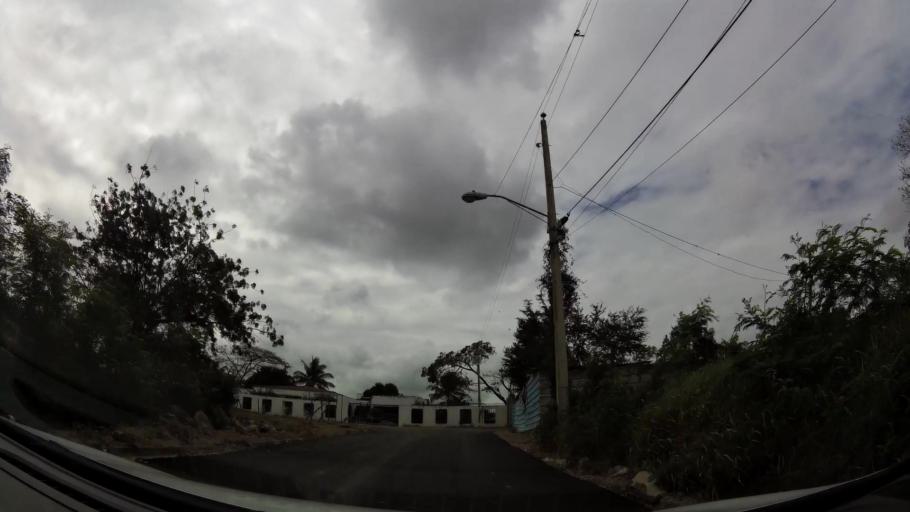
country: DO
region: Santiago
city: Santiago de los Caballeros
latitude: 19.4353
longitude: -70.6716
